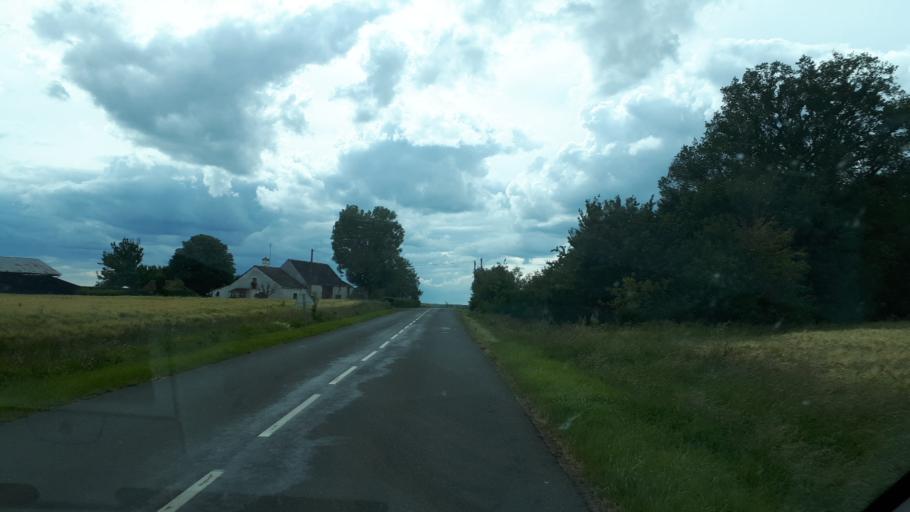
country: FR
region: Centre
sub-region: Departement du Cher
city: Gracay
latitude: 47.1254
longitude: 1.9158
